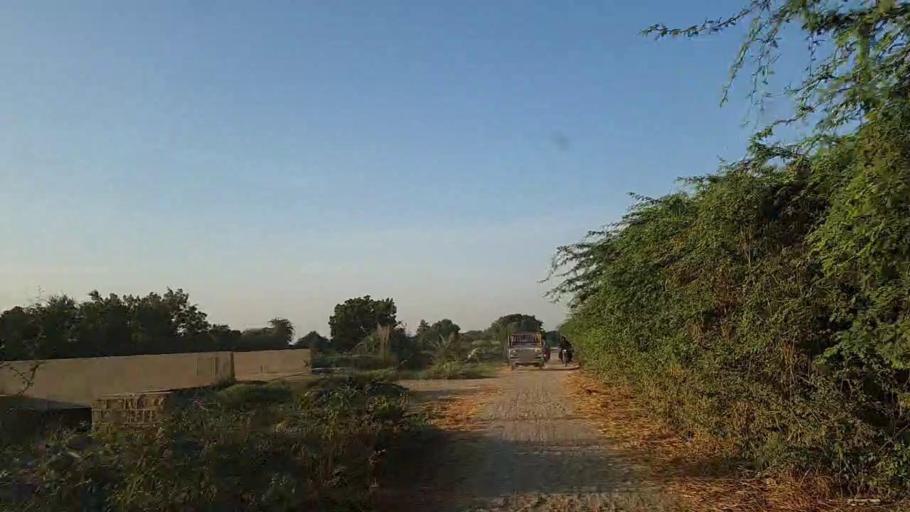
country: PK
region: Sindh
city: Mirpur Batoro
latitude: 24.7093
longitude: 68.2151
